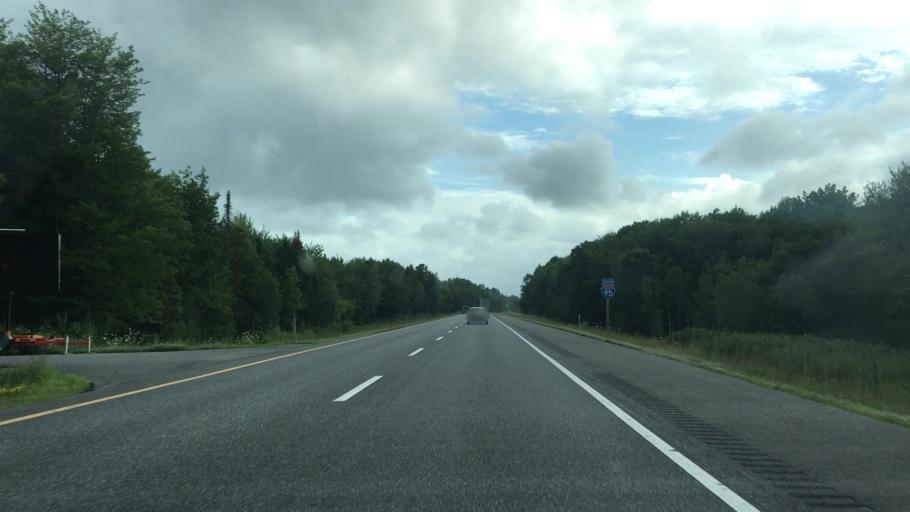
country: US
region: Maine
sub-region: Kennebec County
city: Clinton
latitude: 44.6343
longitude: -69.5343
